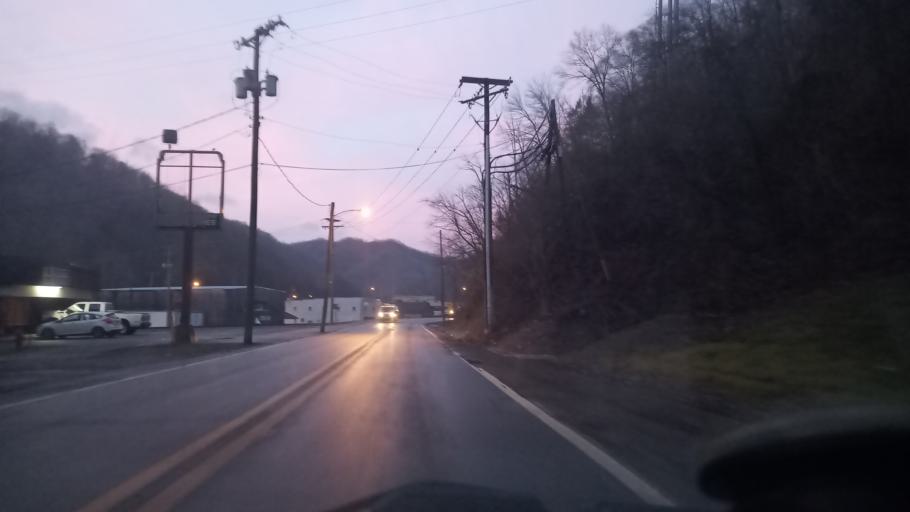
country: US
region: West Virginia
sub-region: Logan County
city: Mallory
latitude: 37.7409
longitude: -81.8759
